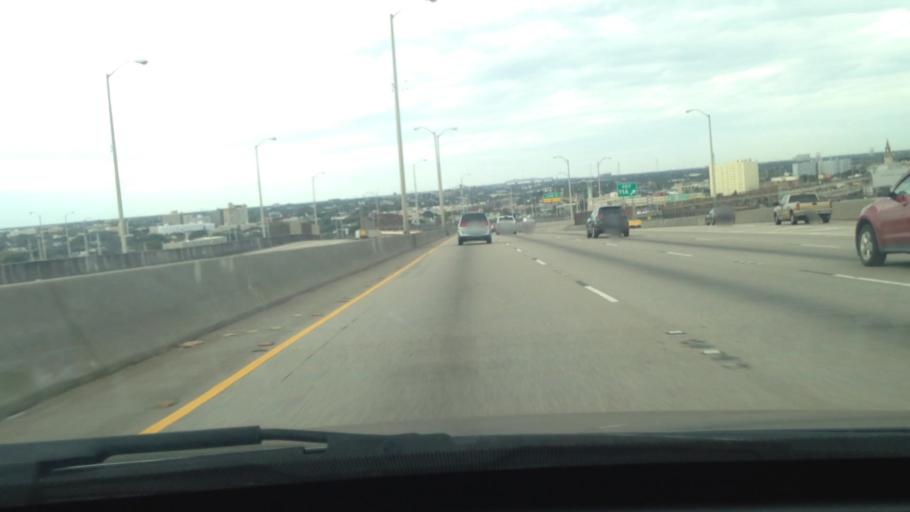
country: US
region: Louisiana
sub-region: Orleans Parish
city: New Orleans
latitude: 29.9388
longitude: -90.0628
